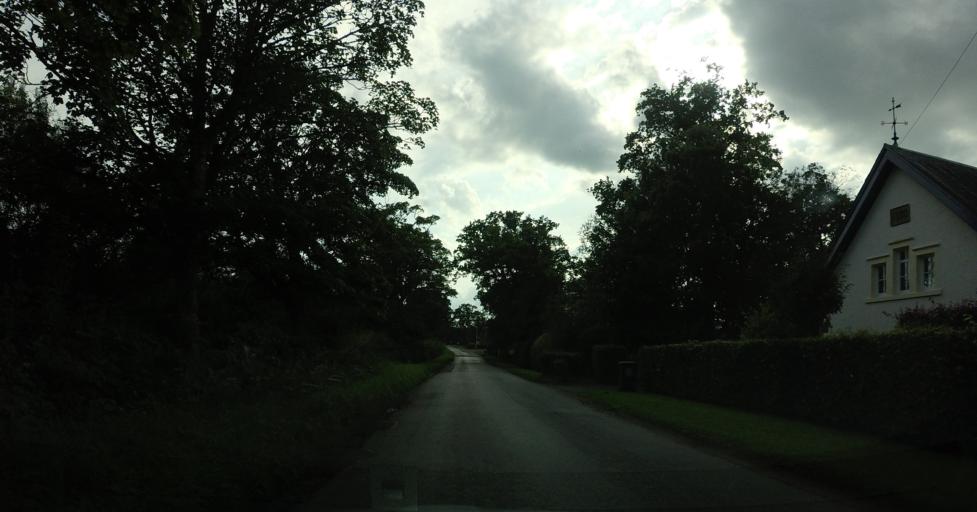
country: GB
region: Scotland
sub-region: Perth and Kinross
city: Auchterarder
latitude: 56.3064
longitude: -3.7414
